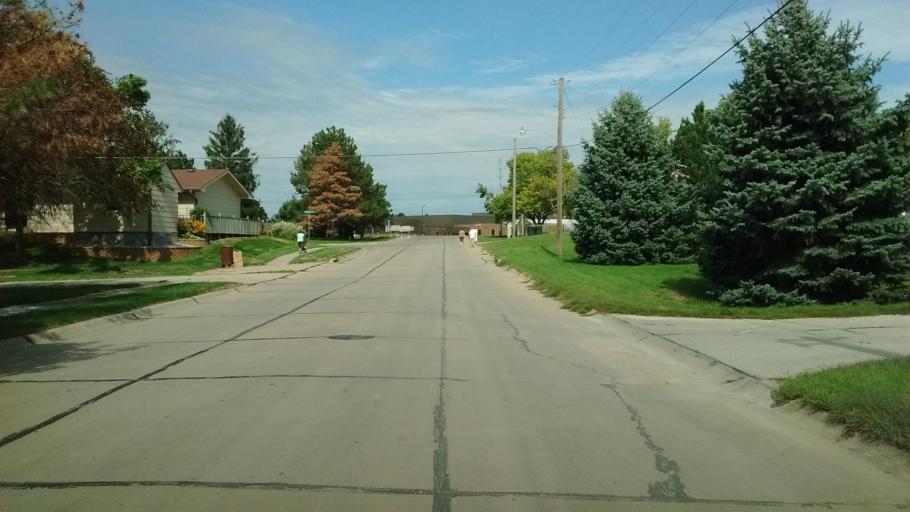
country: US
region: South Dakota
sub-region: Union County
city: North Sioux City
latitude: 42.5468
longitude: -96.5236
